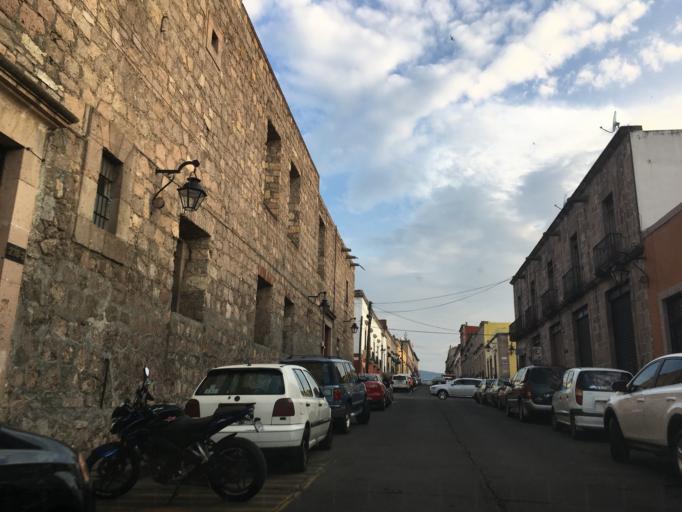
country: MX
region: Michoacan
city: Morelia
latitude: 19.7052
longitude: -101.1932
